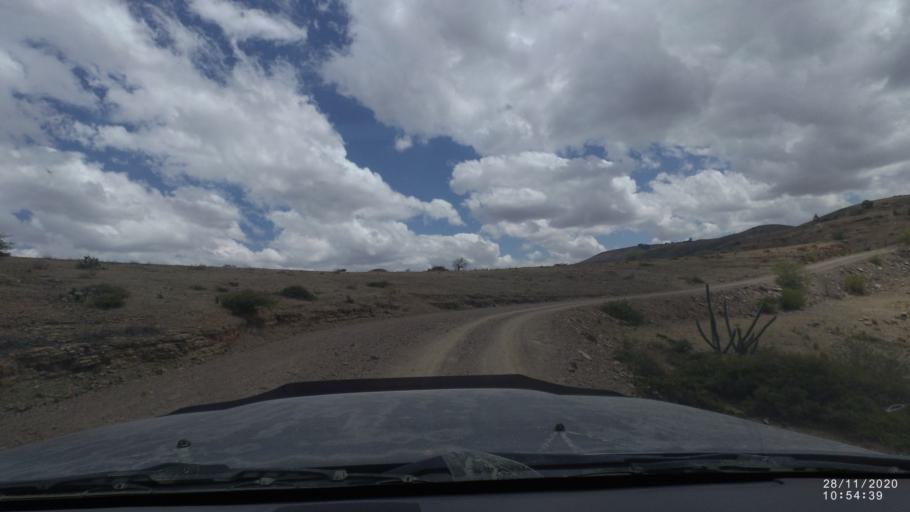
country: BO
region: Cochabamba
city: Capinota
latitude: -17.7770
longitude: -66.1194
